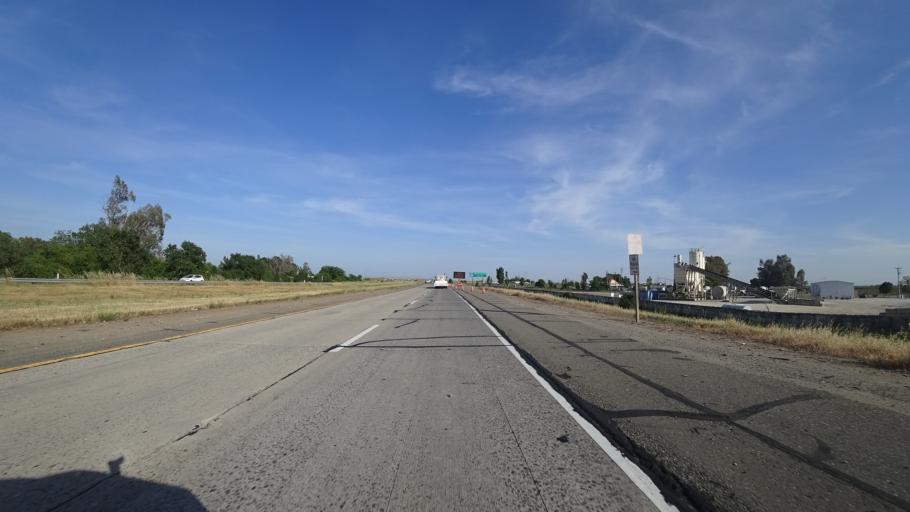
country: US
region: California
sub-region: Yuba County
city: Olivehurst
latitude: 39.0704
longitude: -121.5217
